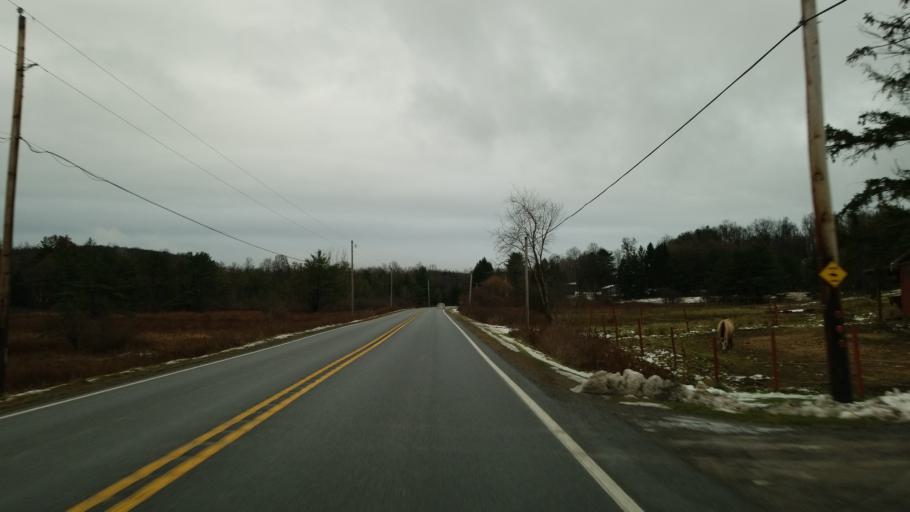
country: US
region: Pennsylvania
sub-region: Clearfield County
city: DuBois
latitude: 41.1037
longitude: -78.7136
